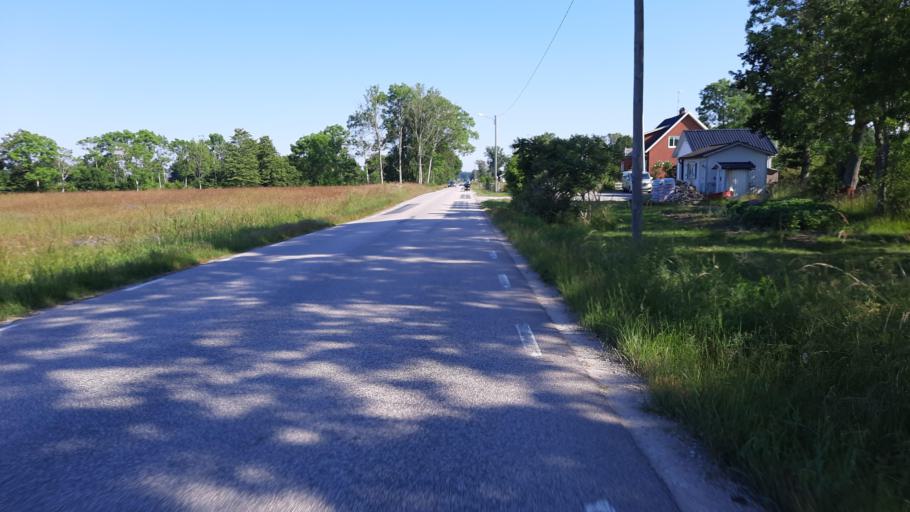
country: SE
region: Blekinge
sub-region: Karlskrona Kommun
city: Sturko
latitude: 56.1095
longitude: 15.6833
